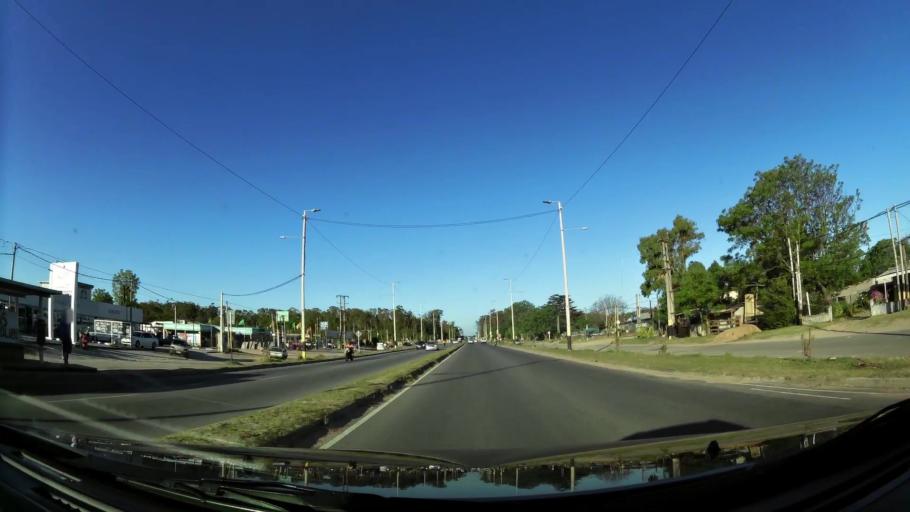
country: UY
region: Canelones
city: Paso de Carrasco
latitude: -34.8550
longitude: -56.0428
